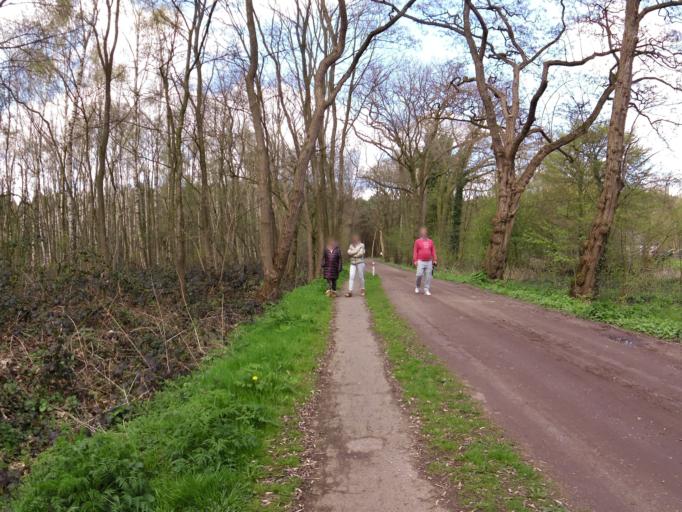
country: NL
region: North Brabant
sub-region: Gemeente Vught
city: Vught
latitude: 51.6325
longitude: 5.2685
